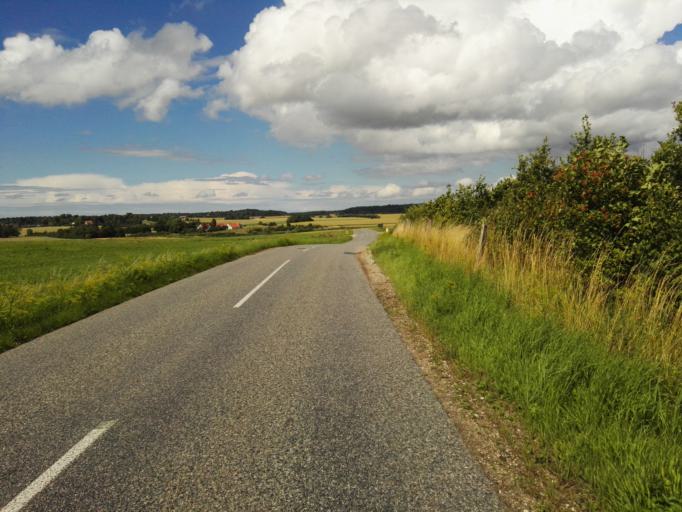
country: DK
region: Capital Region
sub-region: Egedal Kommune
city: Ganlose
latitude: 55.7865
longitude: 12.2342
